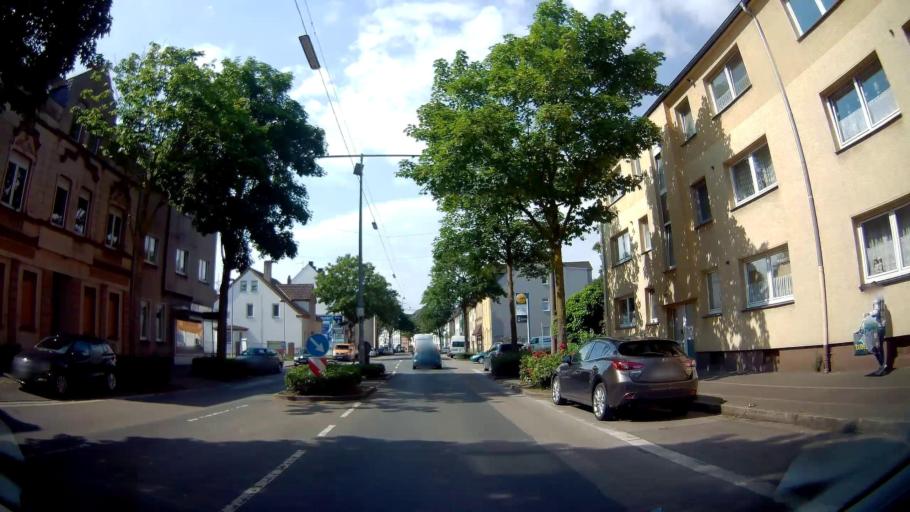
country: DE
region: North Rhine-Westphalia
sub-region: Regierungsbezirk Arnsberg
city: Herne
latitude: 51.5656
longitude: 7.2095
